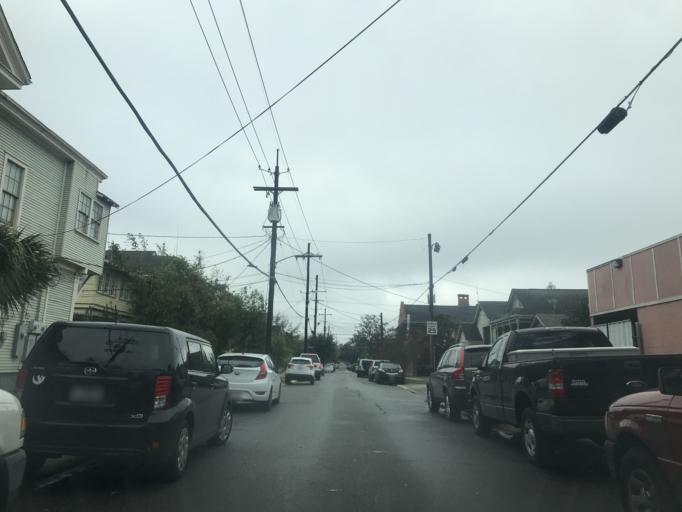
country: US
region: Louisiana
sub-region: Orleans Parish
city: New Orleans
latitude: 29.9723
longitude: -90.0979
